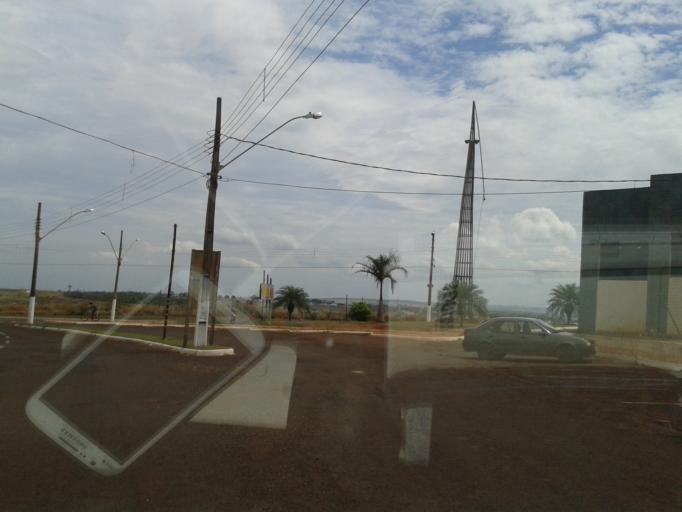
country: BR
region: Goias
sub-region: Itumbiara
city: Itumbiara
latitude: -18.4300
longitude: -49.1913
